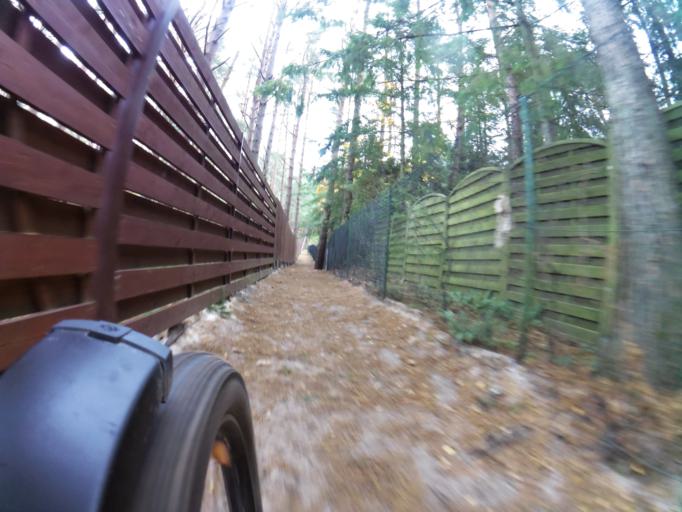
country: PL
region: Pomeranian Voivodeship
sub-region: Powiat pucki
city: Wierzchucino
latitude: 54.8299
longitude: 18.0823
